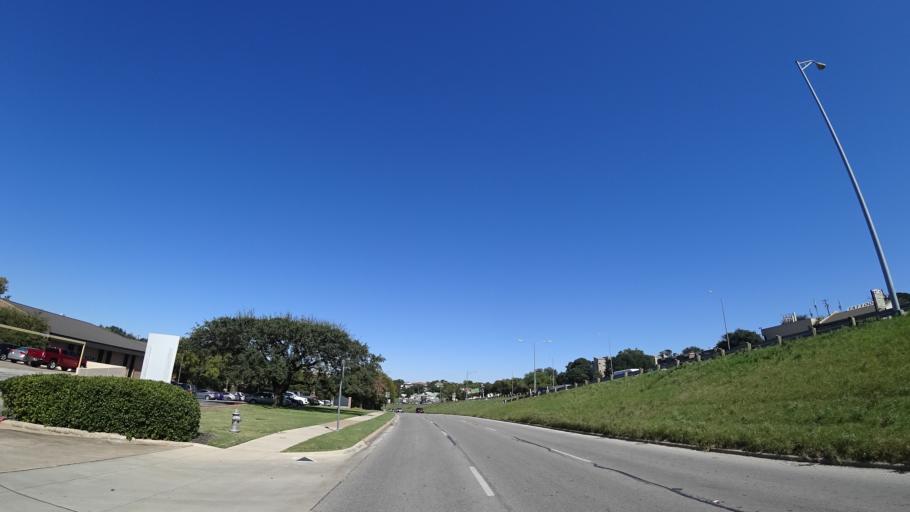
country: US
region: Texas
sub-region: Travis County
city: Austin
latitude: 30.2422
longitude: -97.7366
